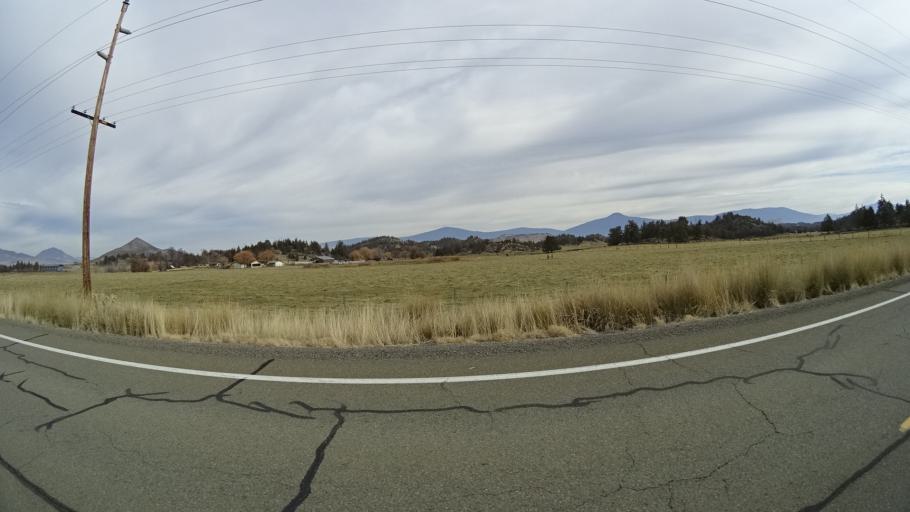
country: US
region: California
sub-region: Siskiyou County
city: Montague
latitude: 41.6797
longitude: -122.5289
